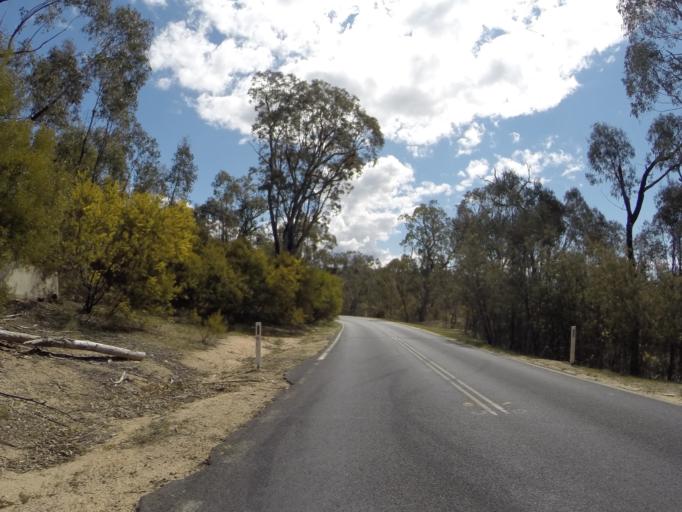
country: AU
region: Australian Capital Territory
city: Macquarie
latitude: -35.3543
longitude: 148.9442
